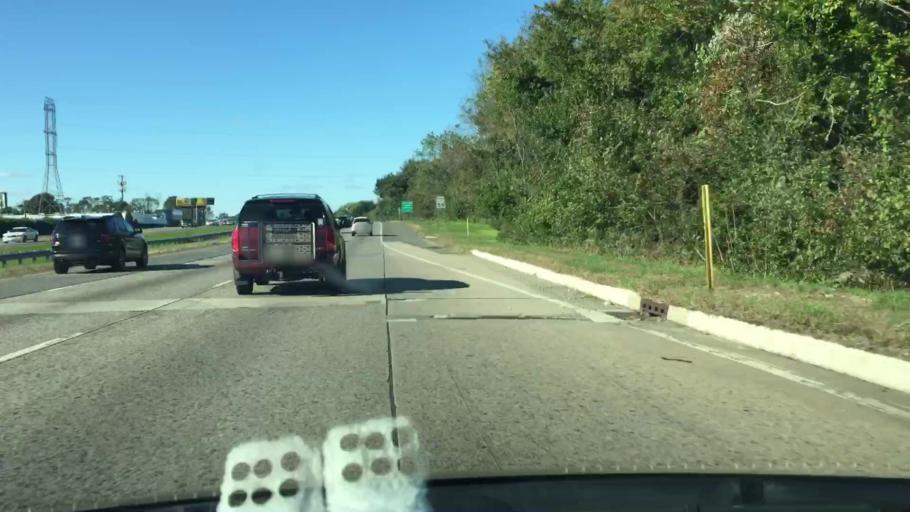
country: US
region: New Jersey
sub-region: Camden County
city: Blackwood
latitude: 39.8061
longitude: -75.0573
